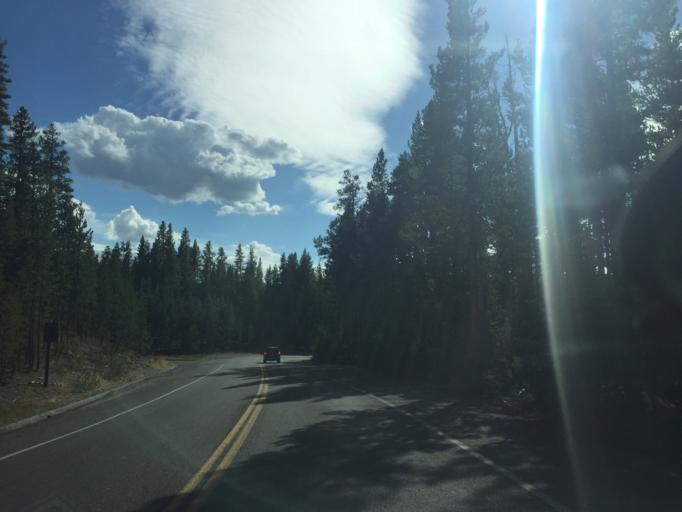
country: US
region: Montana
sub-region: Gallatin County
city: West Yellowstone
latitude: 44.7092
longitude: -110.5010
